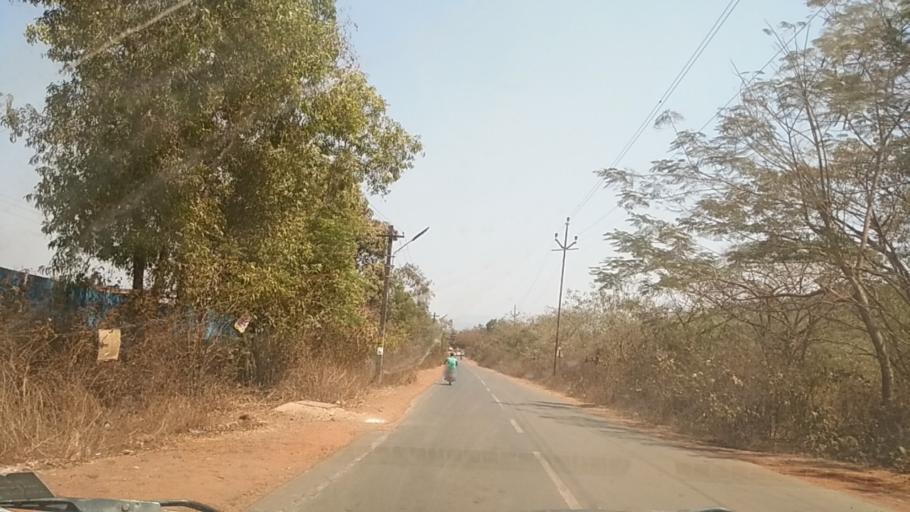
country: IN
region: Goa
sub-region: North Goa
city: Dicholi
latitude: 15.5821
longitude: 73.9381
